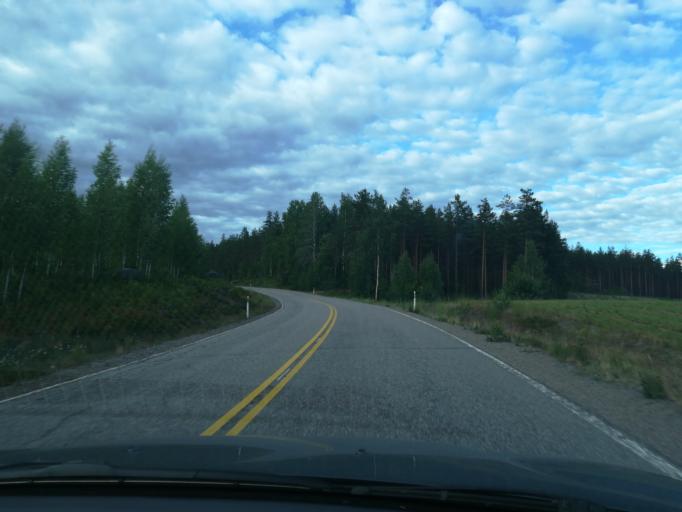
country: FI
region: Southern Savonia
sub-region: Mikkeli
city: Puumala
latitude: 61.5012
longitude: 27.8614
